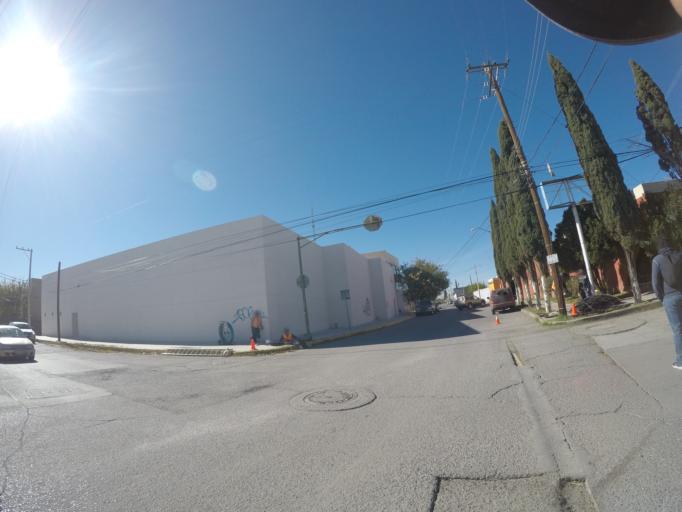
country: MX
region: Chihuahua
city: Ciudad Juarez
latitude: 31.7419
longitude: -106.4554
